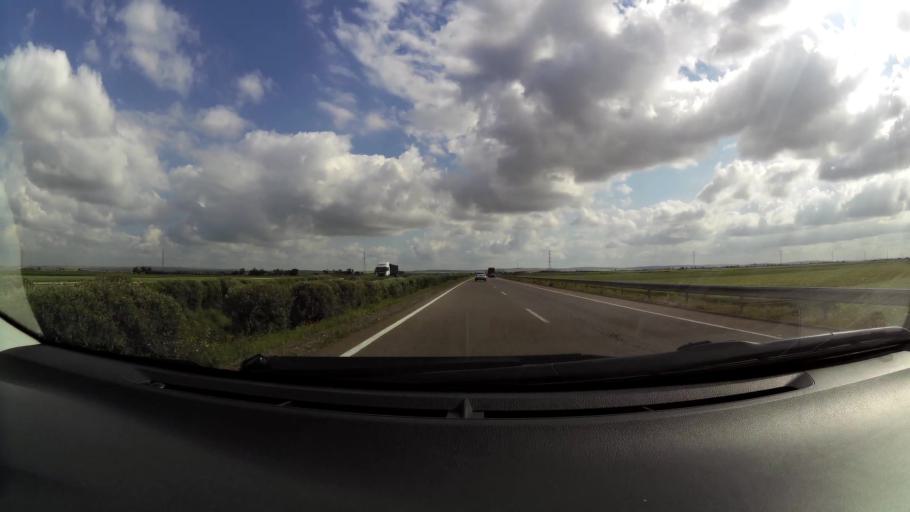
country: MA
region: Chaouia-Ouardigha
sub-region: Settat Province
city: Berrechid
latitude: 33.1615
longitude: -7.5705
